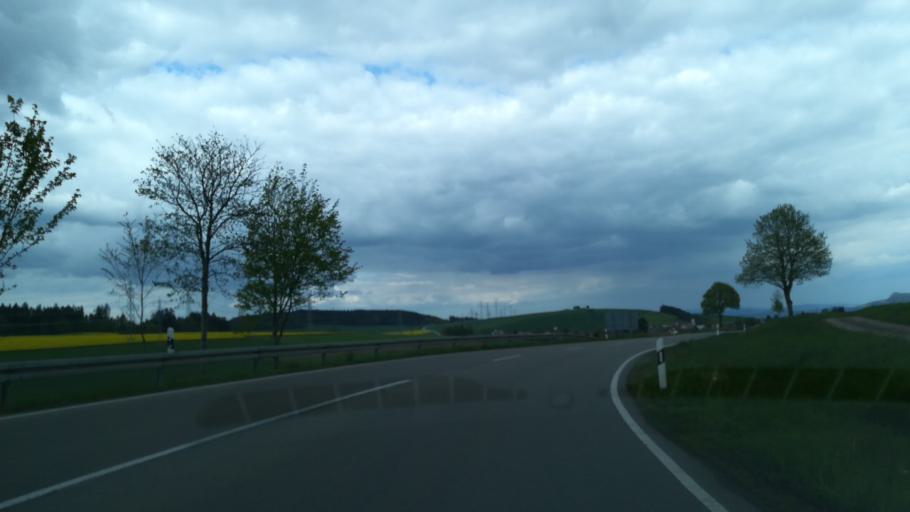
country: DE
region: Baden-Wuerttemberg
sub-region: Freiburg Region
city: Tengen
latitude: 47.8152
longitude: 8.5992
